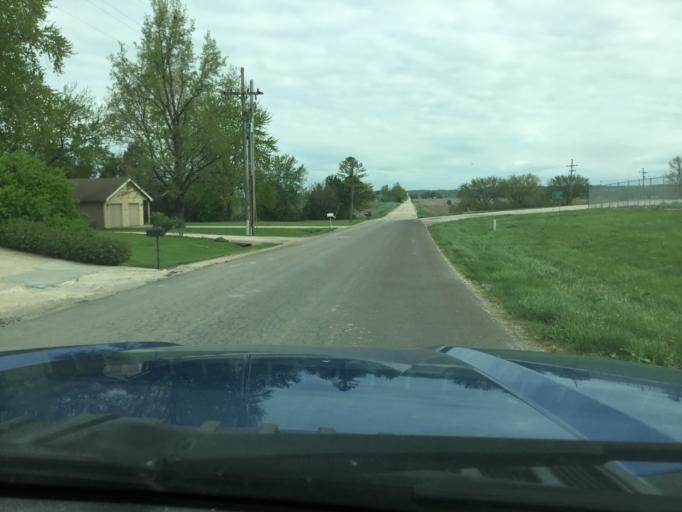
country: US
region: Kansas
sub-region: Douglas County
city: Lawrence
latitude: 39.0043
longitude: -95.2241
